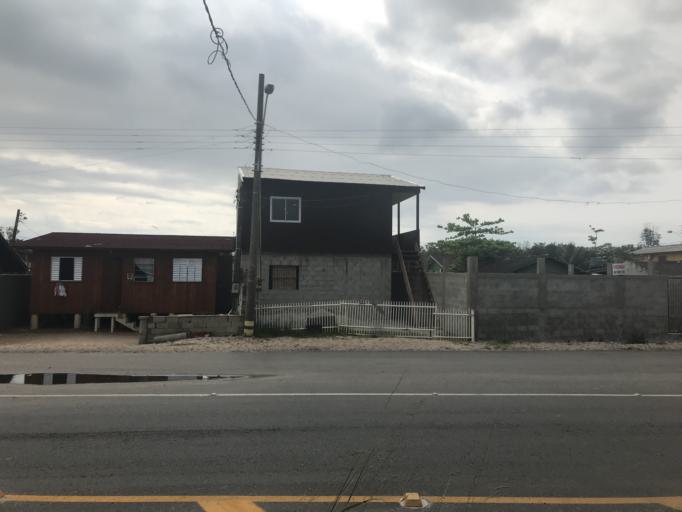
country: BR
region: Santa Catarina
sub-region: Florianopolis
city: Costeira do Pirajubae
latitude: -27.6500
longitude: -48.5221
